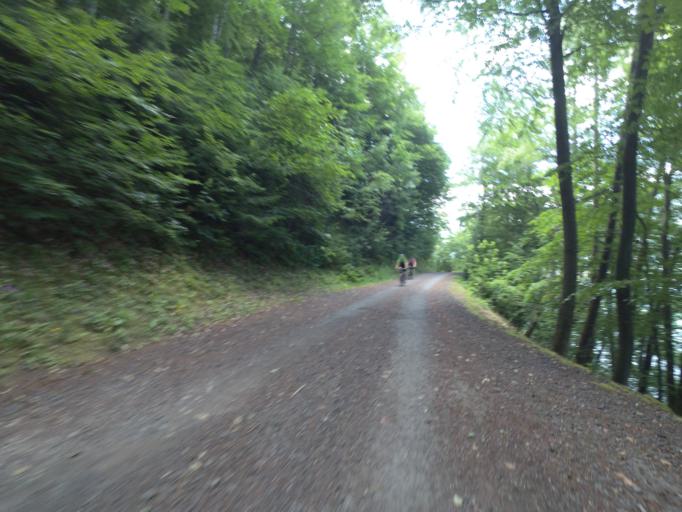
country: AT
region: Carinthia
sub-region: Politischer Bezirk Villach Land
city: Ferndorf
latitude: 46.7680
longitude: 13.6174
